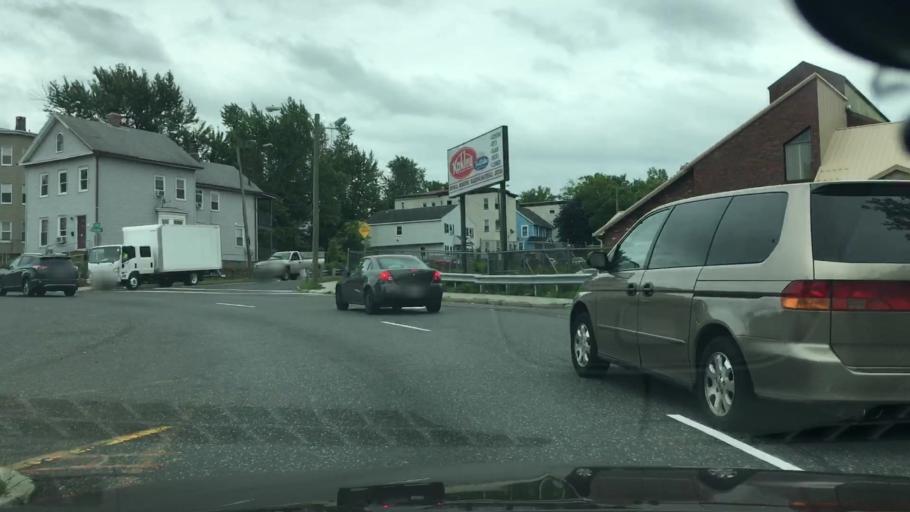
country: US
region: Massachusetts
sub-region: Hampden County
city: Springfield
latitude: 42.0968
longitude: -72.5635
